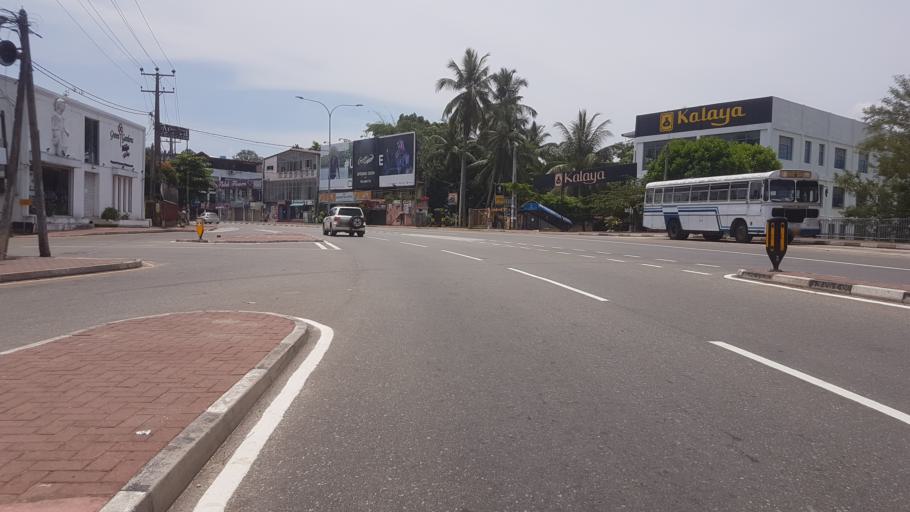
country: LK
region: Western
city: Battaramulla South
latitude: 6.8940
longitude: 79.9251
